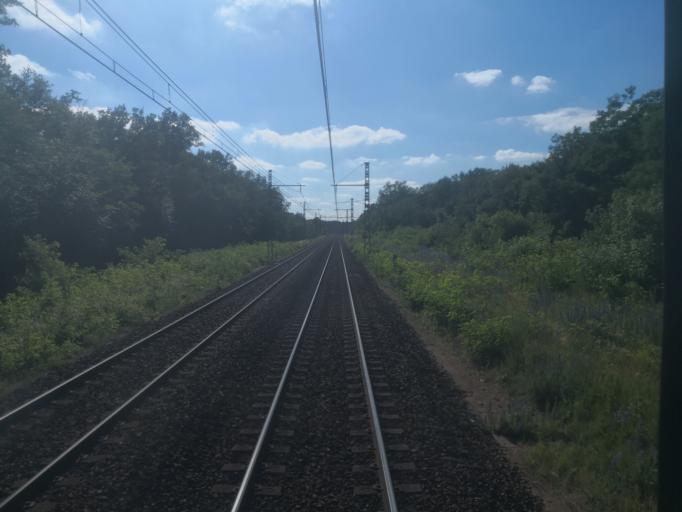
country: FR
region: Ile-de-France
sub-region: Departement de Seine-et-Marne
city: Thomery
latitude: 48.3949
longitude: 2.7563
